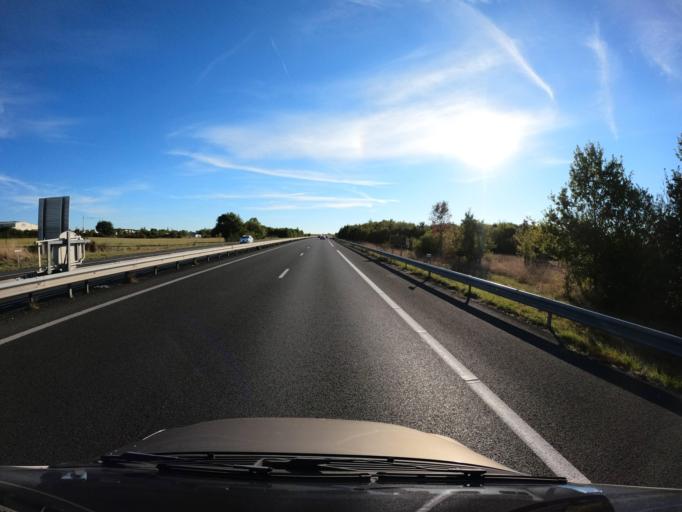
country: FR
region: Pays de la Loire
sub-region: Departement de Maine-et-Loire
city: Moze-sur-Louet
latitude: 47.3715
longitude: -0.5664
